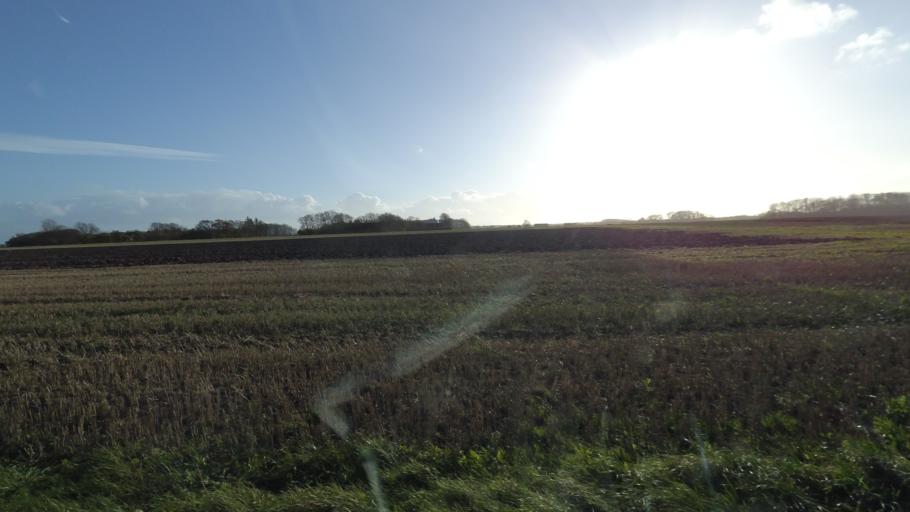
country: DK
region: Central Jutland
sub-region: Odder Kommune
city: Odder
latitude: 55.8787
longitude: 10.1866
